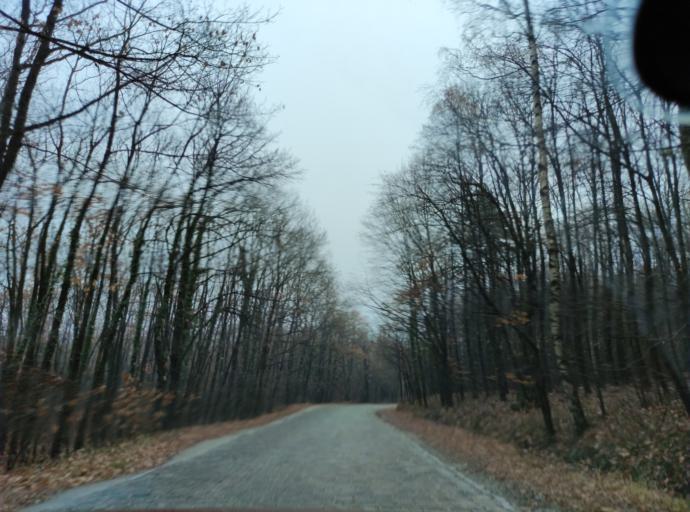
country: BG
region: Sofia-Capital
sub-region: Stolichna Obshtina
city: Sofia
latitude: 42.6221
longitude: 23.3061
